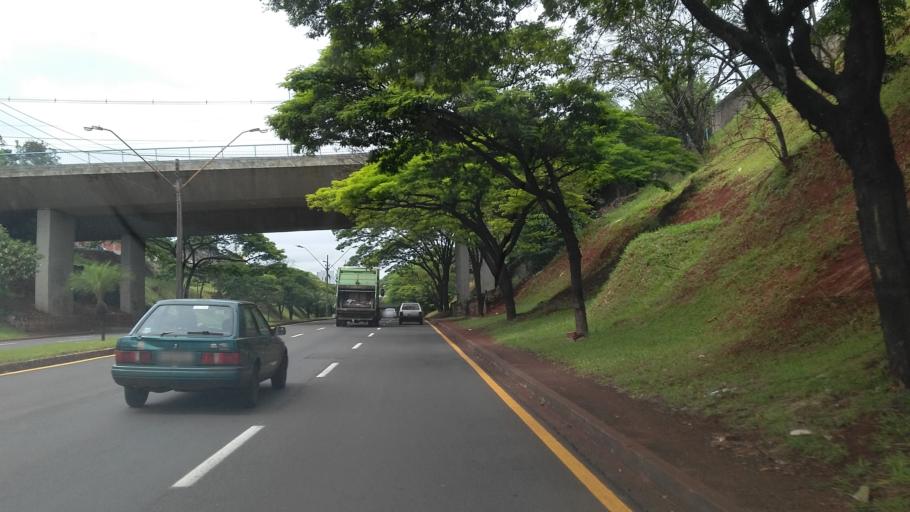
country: BR
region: Parana
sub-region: Londrina
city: Londrina
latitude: -23.3137
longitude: -51.1499
